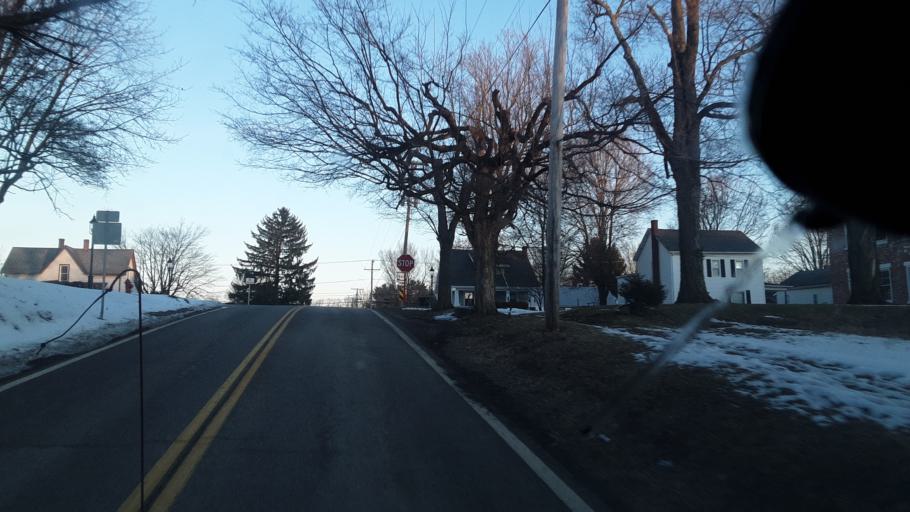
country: US
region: Ohio
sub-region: Perry County
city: Somerset
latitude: 39.8053
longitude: -82.3015
